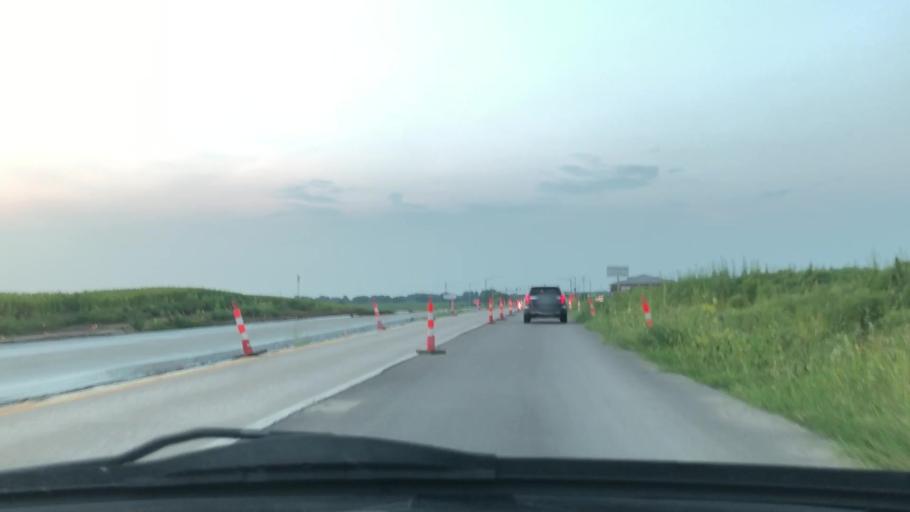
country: US
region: Iowa
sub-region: Johnson County
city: North Liberty
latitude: 41.7198
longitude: -91.6079
